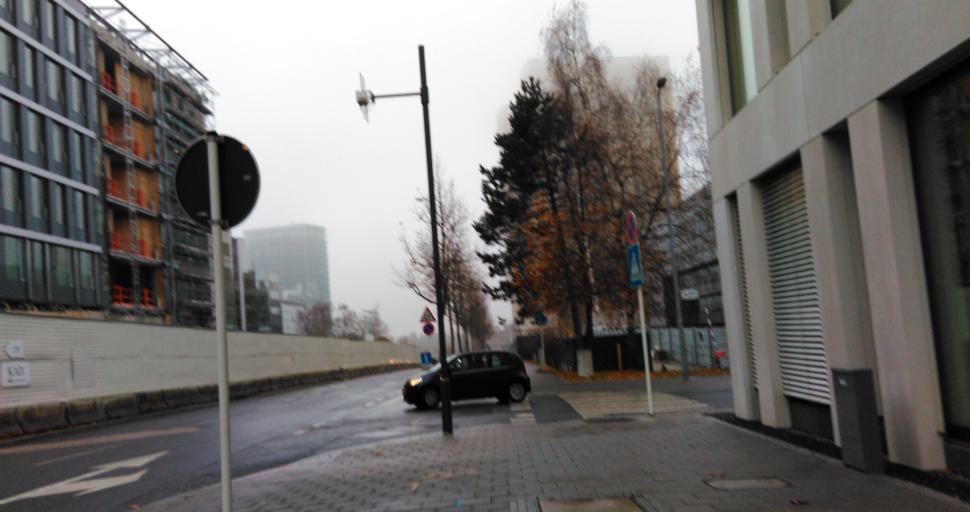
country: LU
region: Luxembourg
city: Kirchberg
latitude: 49.6230
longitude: 6.1474
